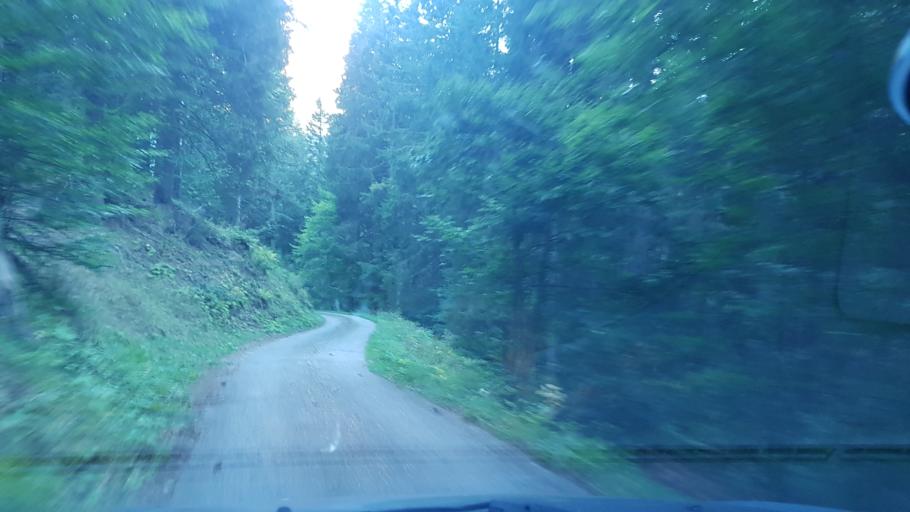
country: IT
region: Veneto
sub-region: Provincia di Belluno
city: Fusine
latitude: 46.3512
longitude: 12.0900
